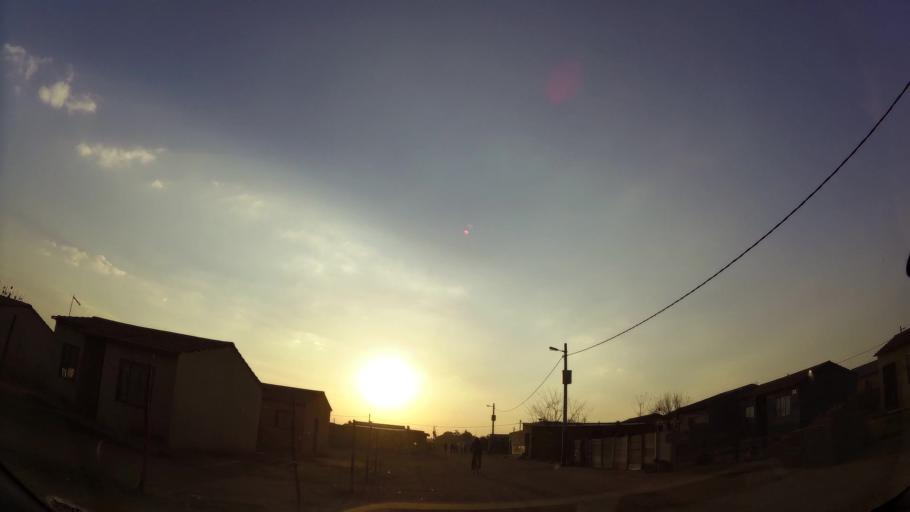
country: ZA
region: Gauteng
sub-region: Ekurhuleni Metropolitan Municipality
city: Benoni
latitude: -26.1621
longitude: 28.3757
